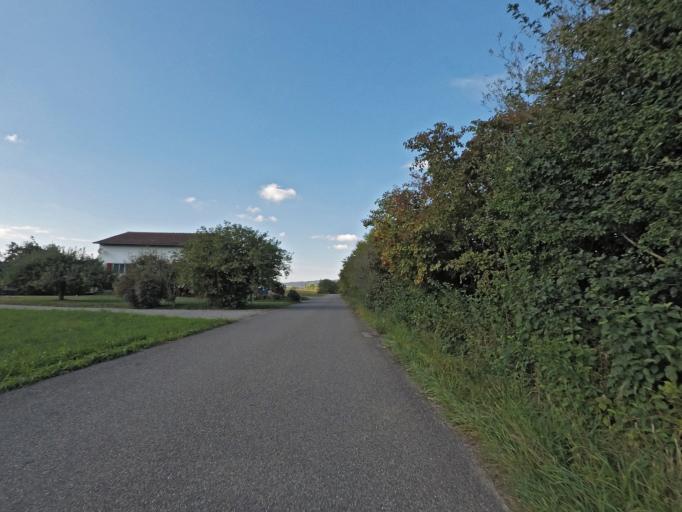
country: CH
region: Thurgau
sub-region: Frauenfeld District
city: Diessenhofen
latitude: 47.6581
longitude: 8.7473
